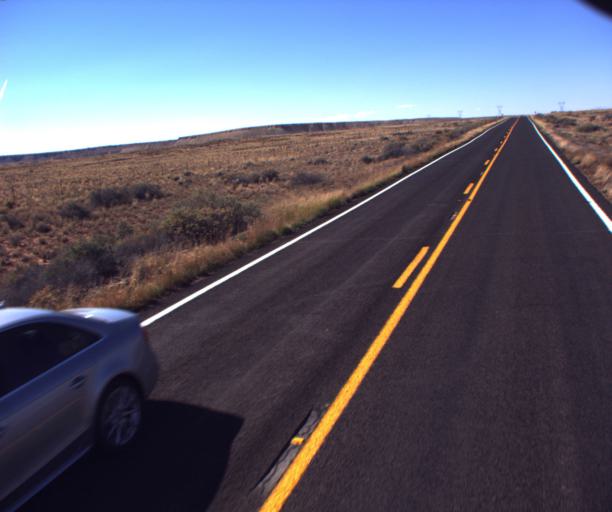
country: US
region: Arizona
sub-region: Coconino County
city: Tuba City
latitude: 35.9701
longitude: -110.8191
